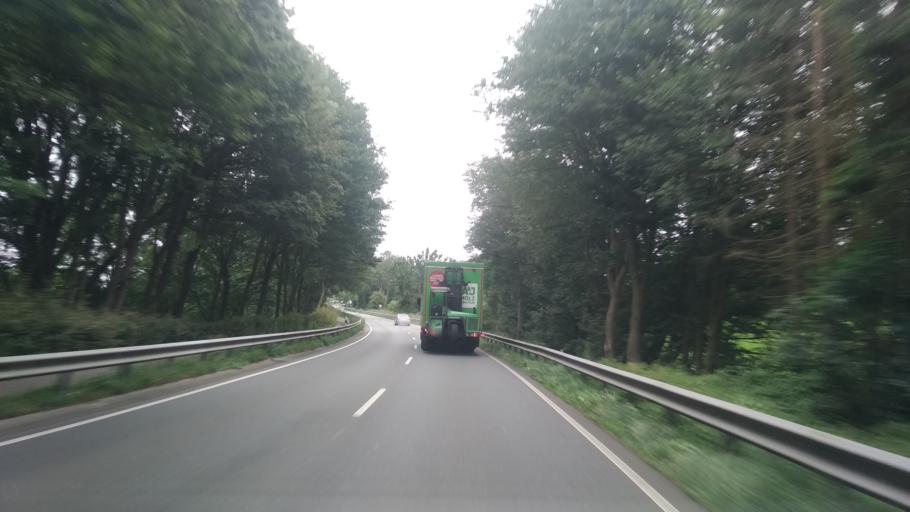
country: DE
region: Schleswig-Holstein
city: Munkbrarup
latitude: 54.8058
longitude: 9.5627
